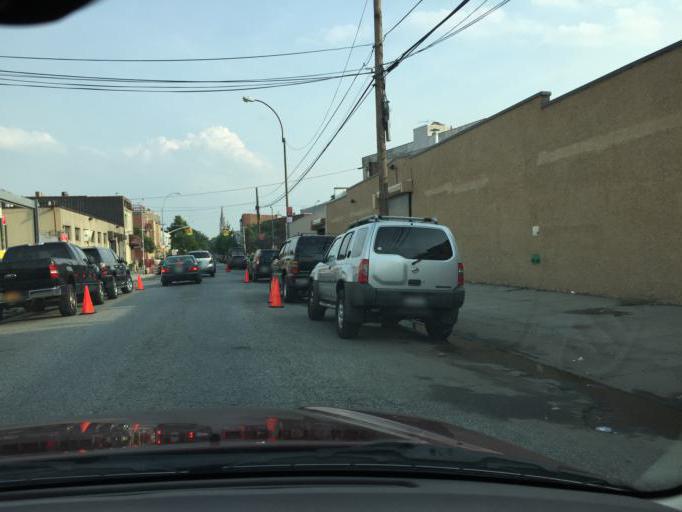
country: US
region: New York
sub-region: Queens County
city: Long Island City
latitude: 40.7282
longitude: -73.9459
